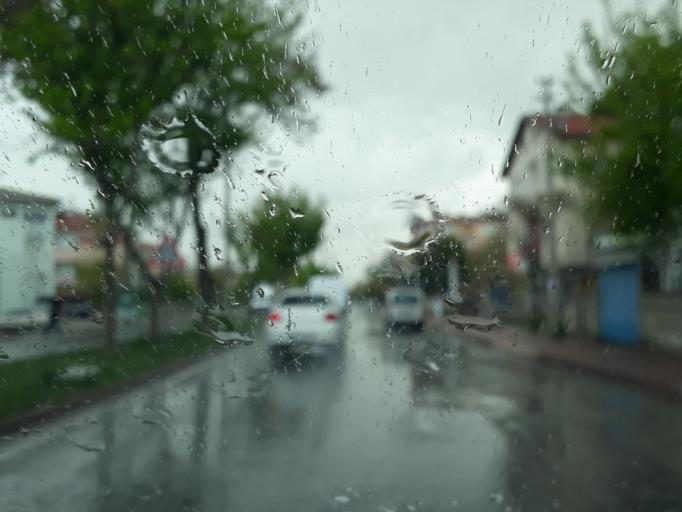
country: TR
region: Konya
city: Selcuklu
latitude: 37.9146
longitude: 32.4945
